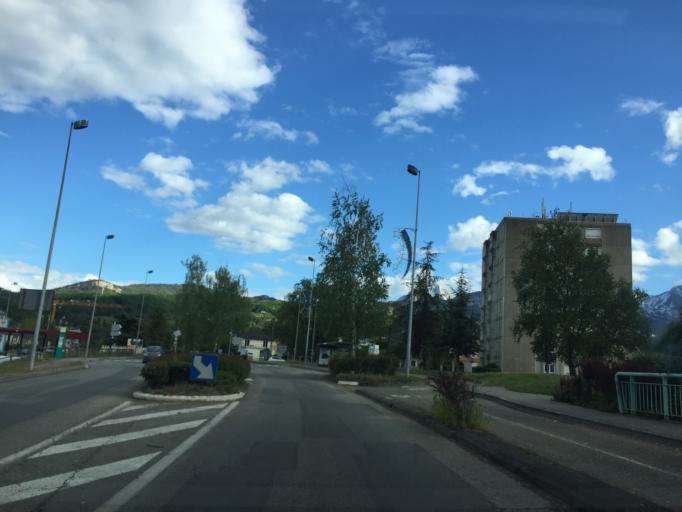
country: FR
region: Rhone-Alpes
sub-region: Departement de la Savoie
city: Cognin
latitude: 45.5603
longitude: 5.8950
